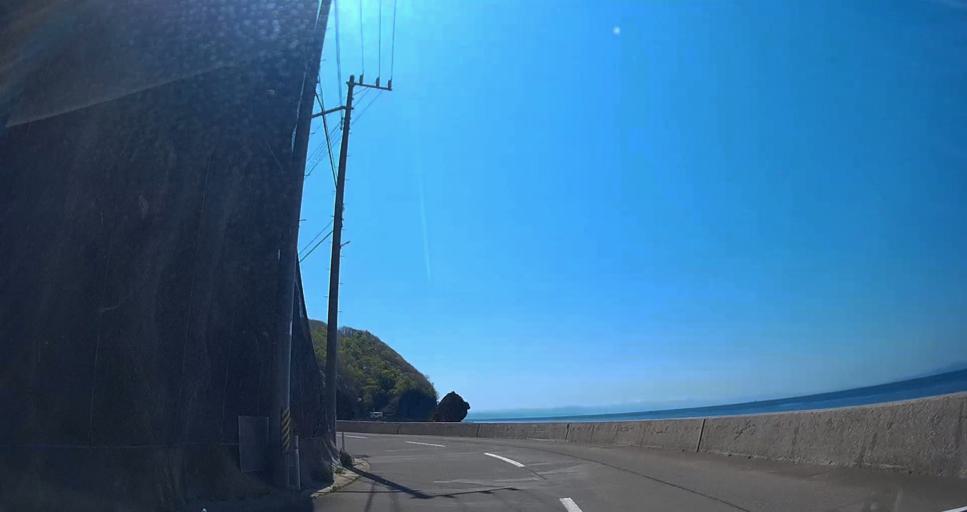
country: JP
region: Aomori
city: Aomori Shi
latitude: 41.1390
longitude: 140.7753
